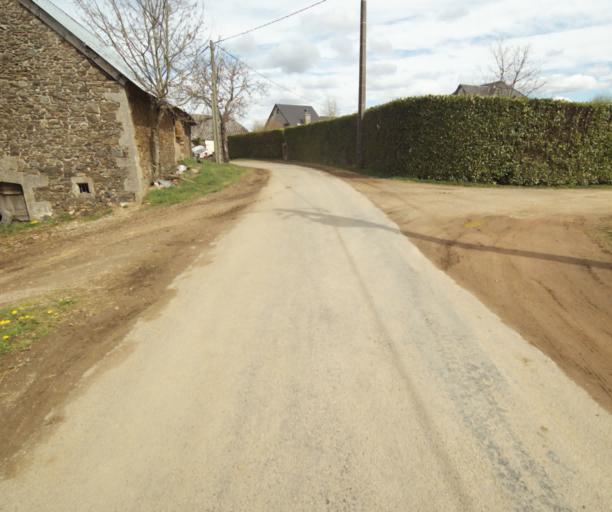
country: FR
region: Limousin
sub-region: Departement de la Correze
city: Laguenne
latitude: 45.2427
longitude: 1.8357
